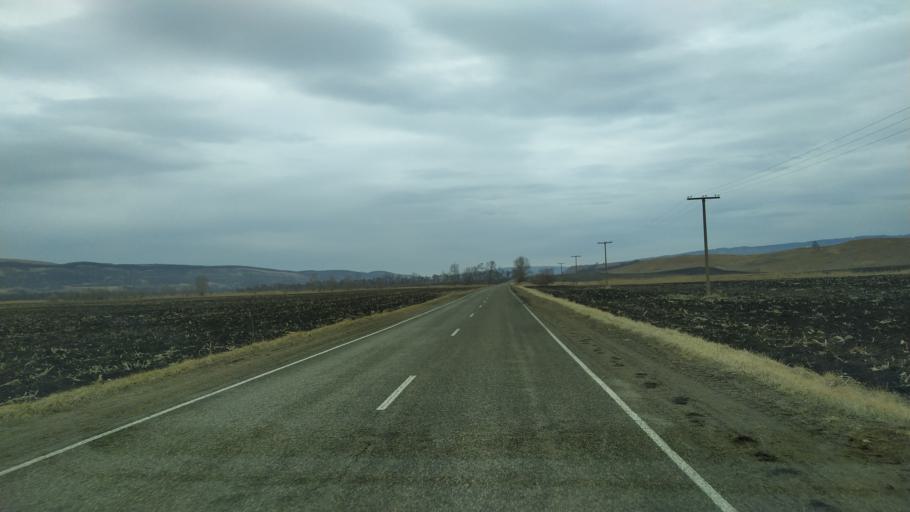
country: RU
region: Krasnodarskiy
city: Peredovaya
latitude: 44.0933
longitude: 41.3871
